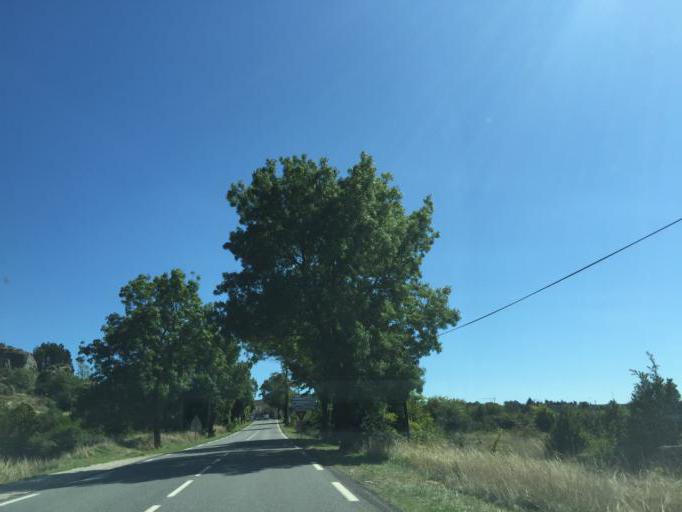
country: FR
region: Languedoc-Roussillon
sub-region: Departement de l'Herault
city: Lodeve
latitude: 43.8675
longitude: 3.3155
